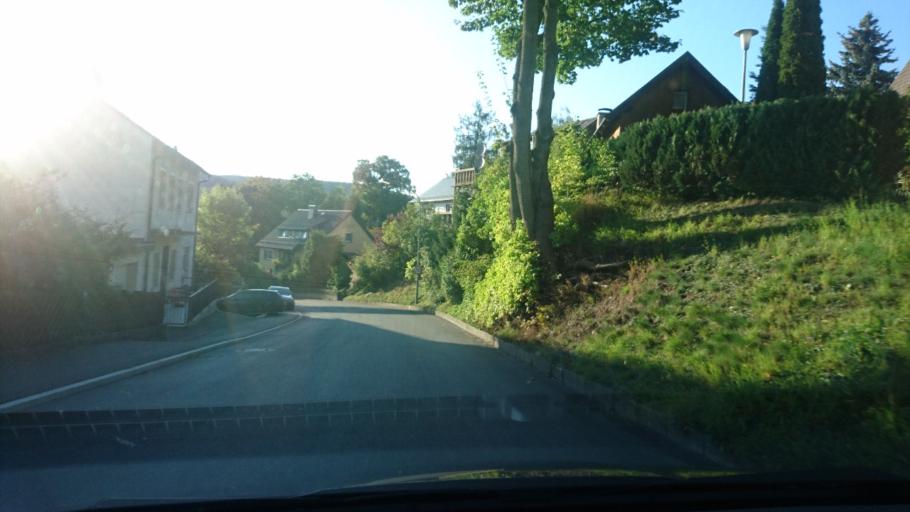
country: DE
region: Bavaria
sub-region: Upper Franconia
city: Naila
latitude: 50.3366
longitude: 11.7111
